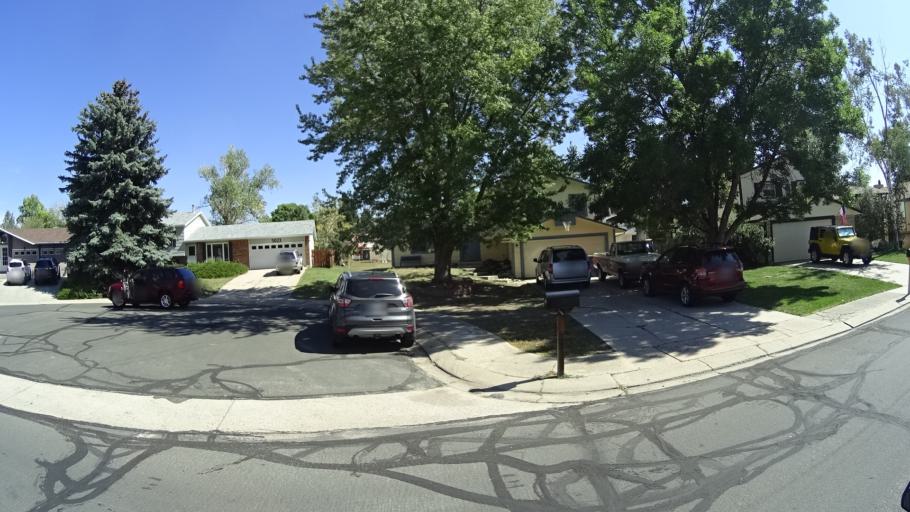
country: US
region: Colorado
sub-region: El Paso County
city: Cimarron Hills
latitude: 38.9053
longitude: -104.7603
